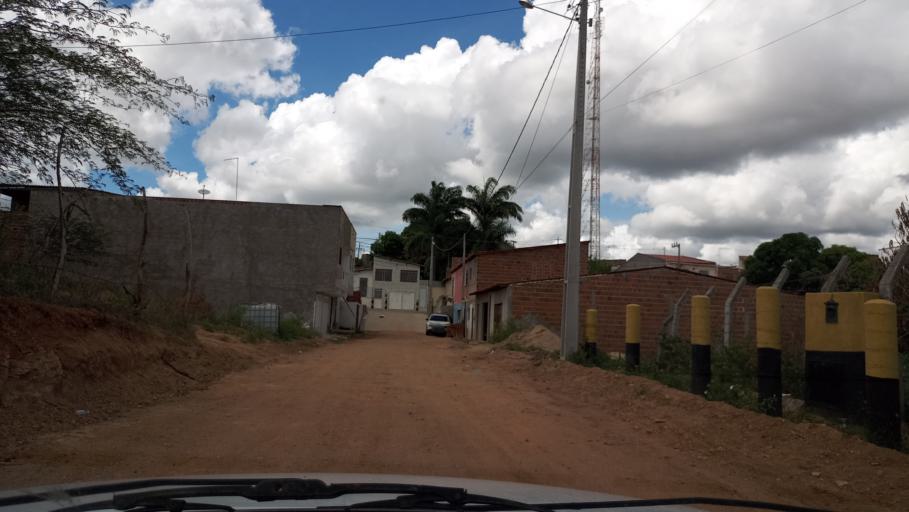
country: BR
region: Rio Grande do Norte
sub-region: Sao Paulo Do Potengi
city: Sao Paulo do Potengi
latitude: -5.8961
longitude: -35.7699
